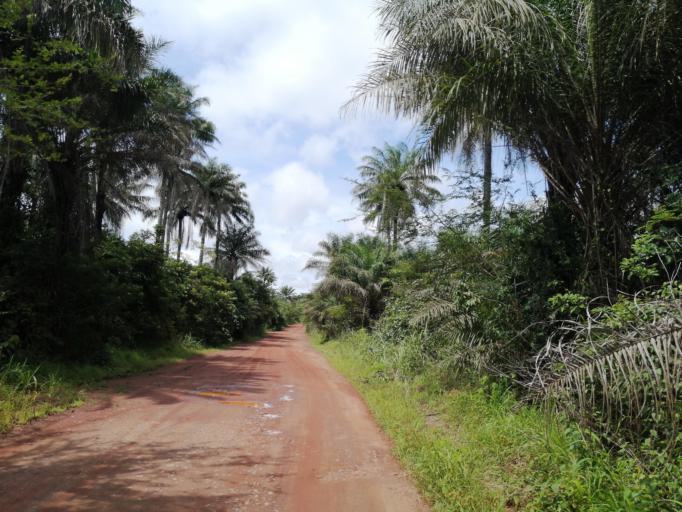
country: SL
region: Northern Province
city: Pepel
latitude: 8.6752
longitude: -13.0006
